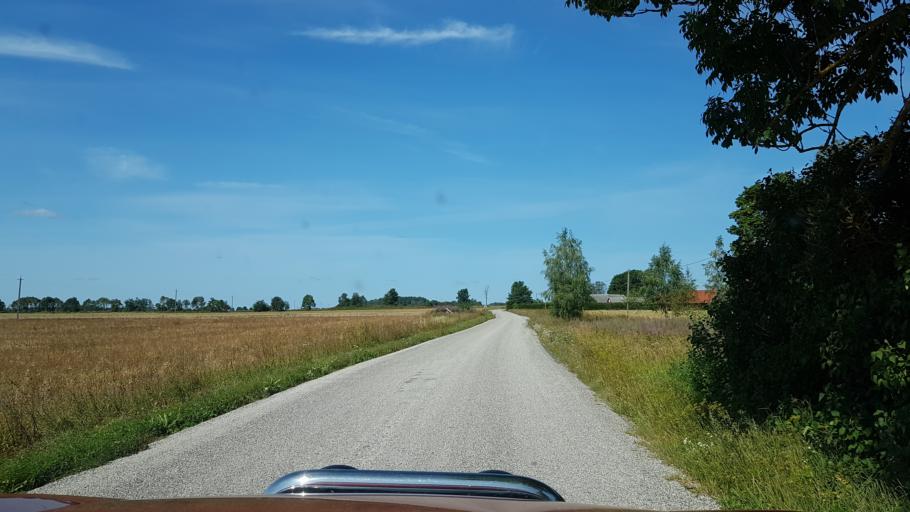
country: EE
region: Jaervamaa
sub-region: Jaerva-Jaani vald
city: Jarva-Jaani
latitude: 59.0839
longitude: 25.7592
